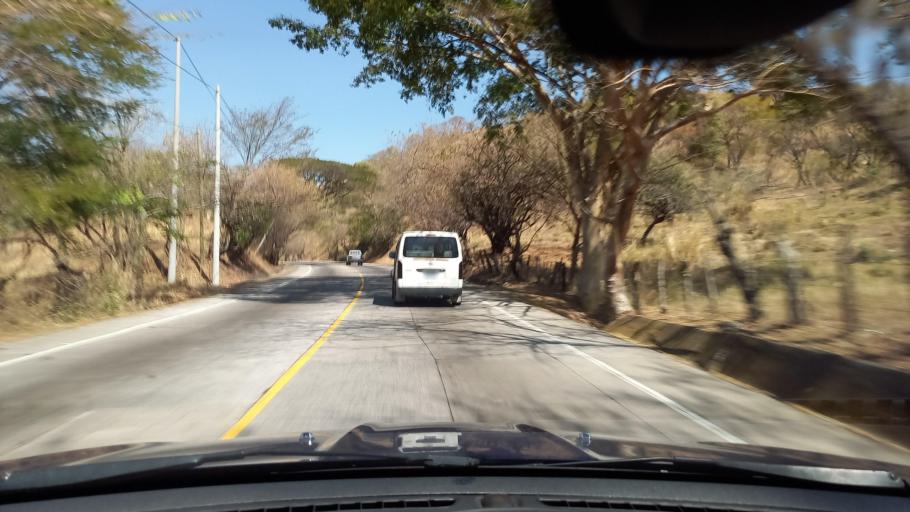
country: SV
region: Santa Ana
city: Texistepeque
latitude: 14.1831
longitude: -89.4938
